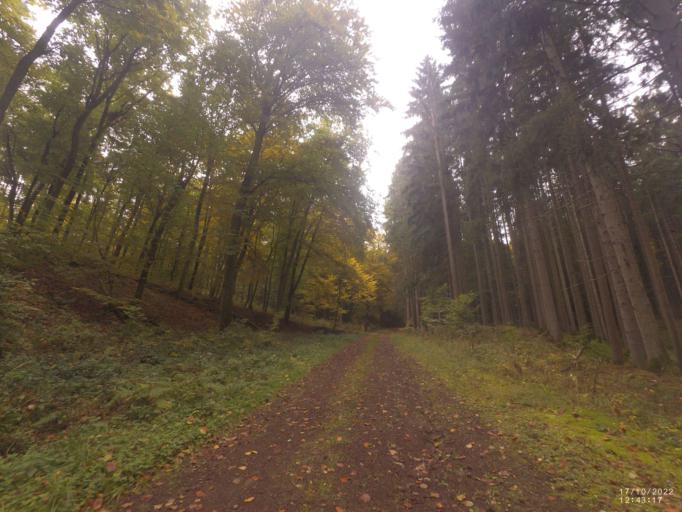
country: DE
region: Rheinland-Pfalz
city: Utzerath
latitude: 50.2109
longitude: 6.9204
